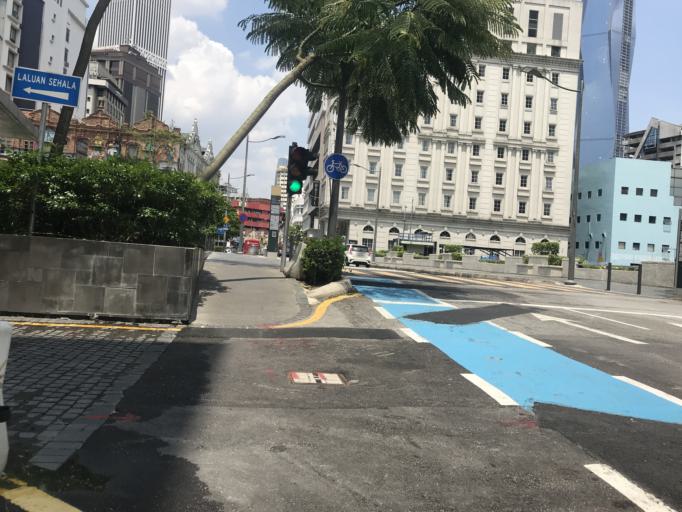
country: MY
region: Kuala Lumpur
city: Kuala Lumpur
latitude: 3.1471
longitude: 101.6949
